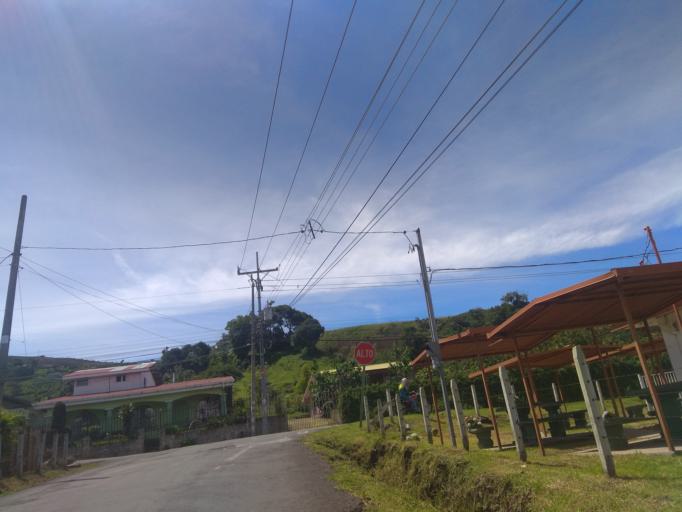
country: CR
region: Cartago
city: Cot
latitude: 9.9211
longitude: -83.8990
